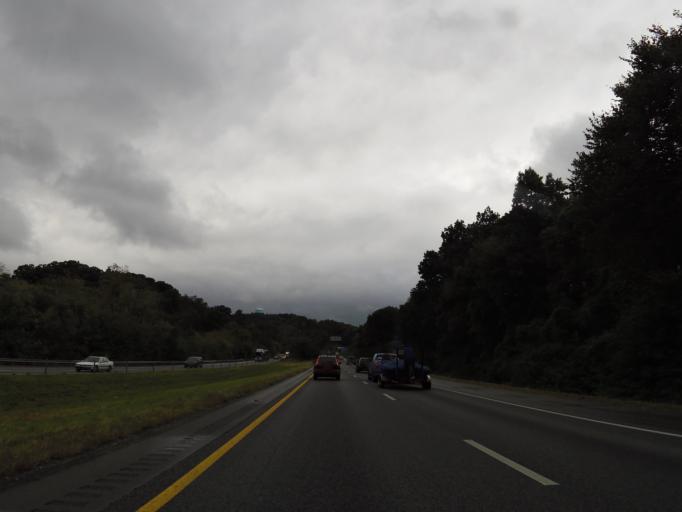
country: US
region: Tennessee
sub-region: Hamilton County
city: Lookout Mountain
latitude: 35.0257
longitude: -85.3728
